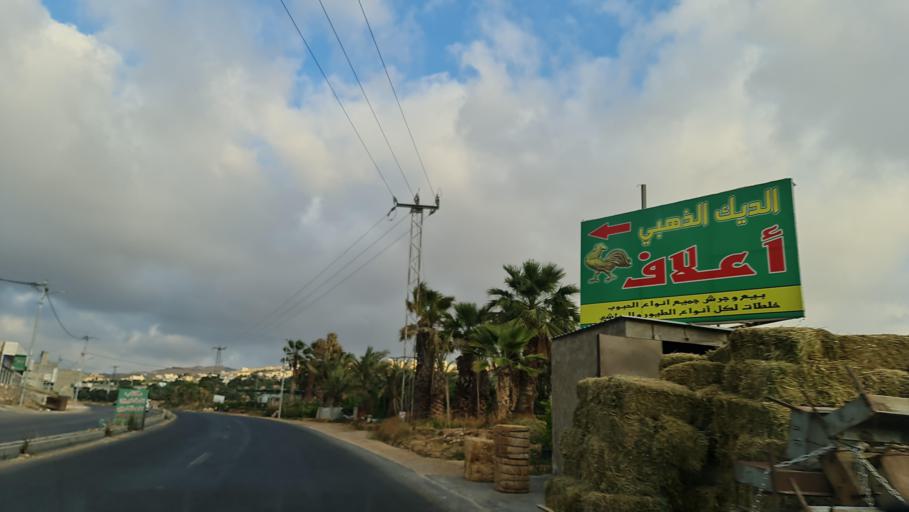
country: JO
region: Amman
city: Al Jubayhah
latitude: 32.0927
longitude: 35.9415
